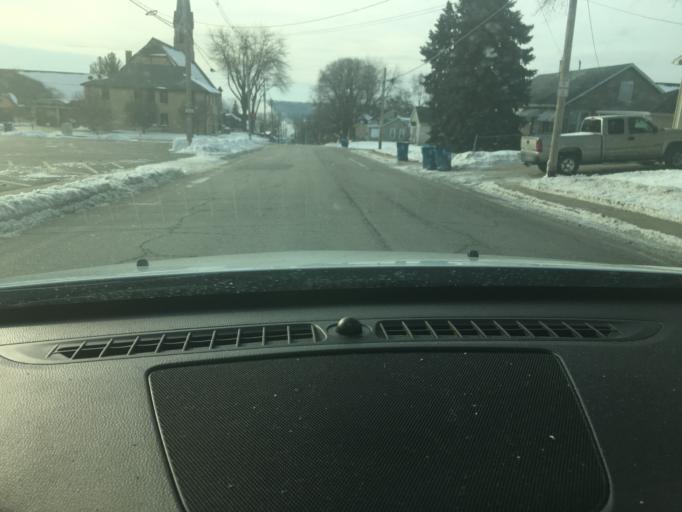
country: US
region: Illinois
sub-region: LaSalle County
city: Peru
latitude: 41.3312
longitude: -89.1131
